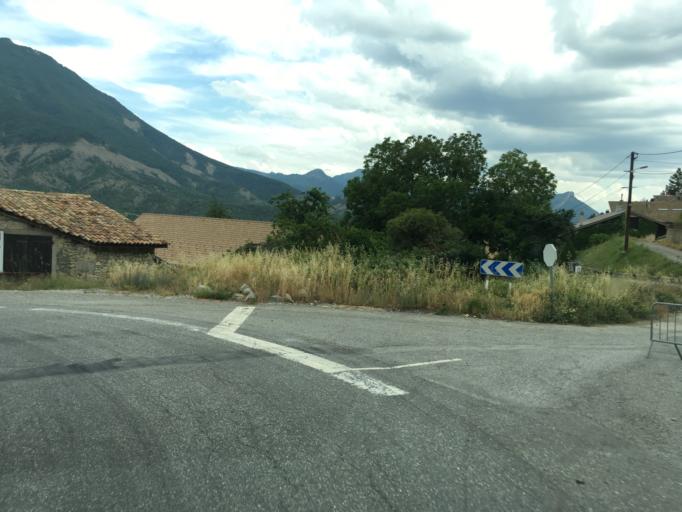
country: FR
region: Provence-Alpes-Cote d'Azur
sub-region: Departement des Hautes-Alpes
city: Veynes
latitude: 44.5305
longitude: 5.8000
